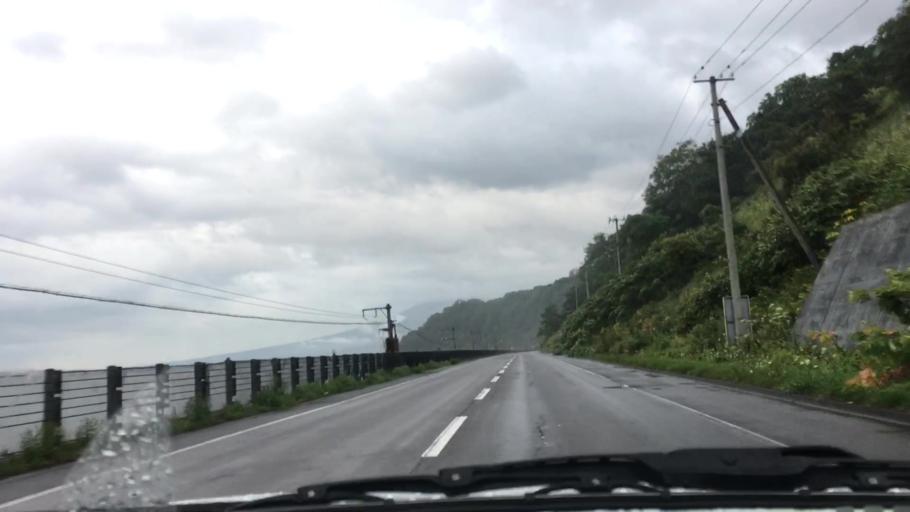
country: JP
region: Hokkaido
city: Nanae
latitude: 42.1245
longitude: 140.5225
